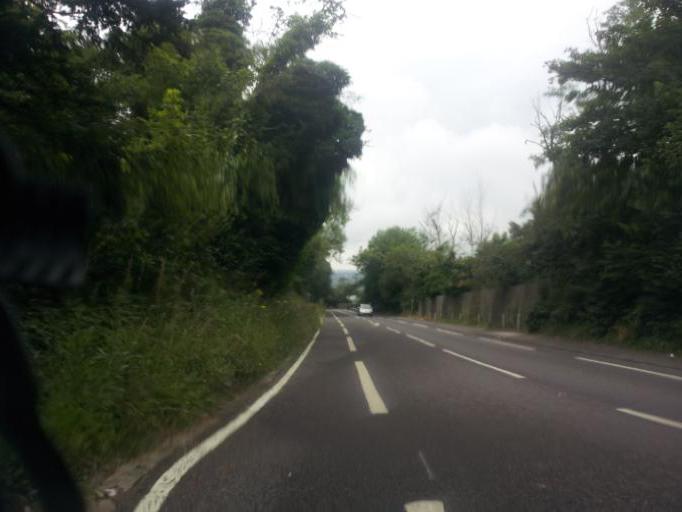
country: GB
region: England
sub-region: Kent
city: Aylesford
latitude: 51.3222
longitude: 0.5058
